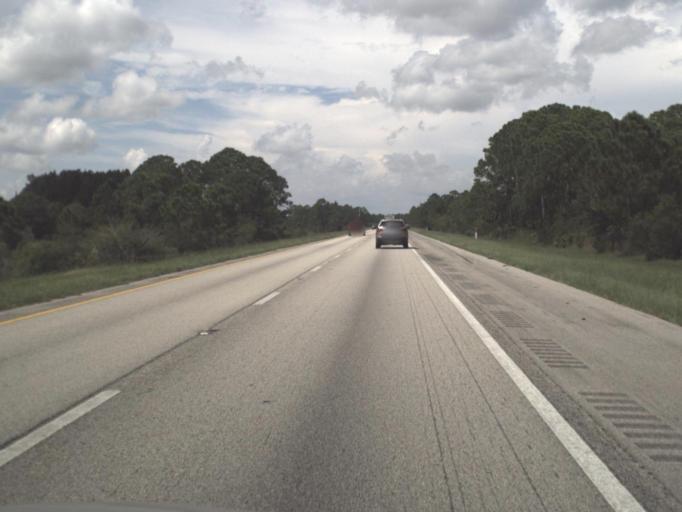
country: US
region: Florida
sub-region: Lee County
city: Suncoast Estates
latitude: 26.7743
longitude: -81.8850
